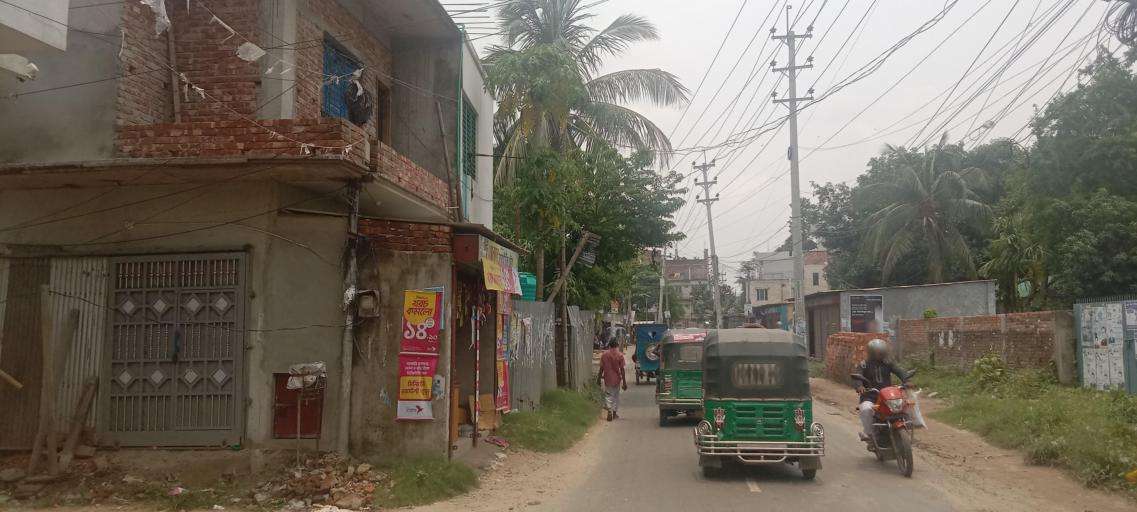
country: BD
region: Dhaka
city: Azimpur
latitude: 23.7310
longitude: 90.3272
